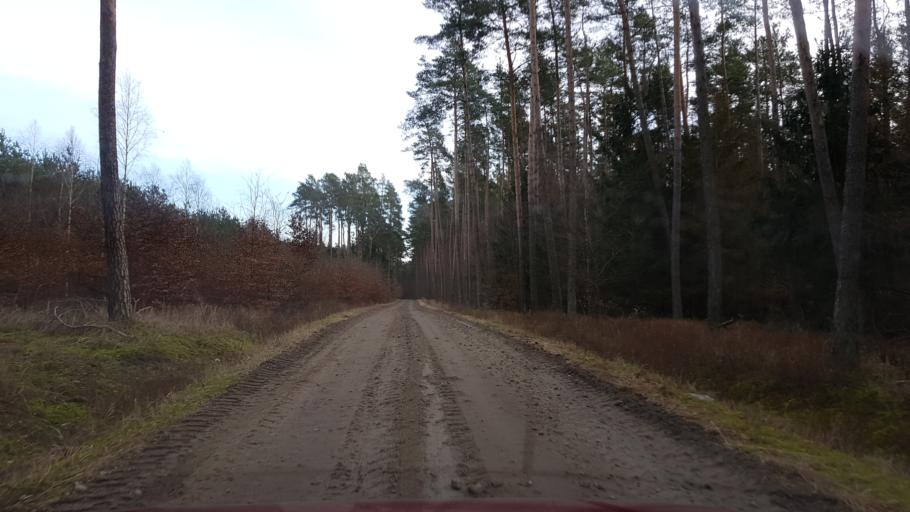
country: PL
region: Lubusz
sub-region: Powiat strzelecko-drezdenecki
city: Strzelce Krajenskie
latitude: 52.9087
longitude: 15.3956
